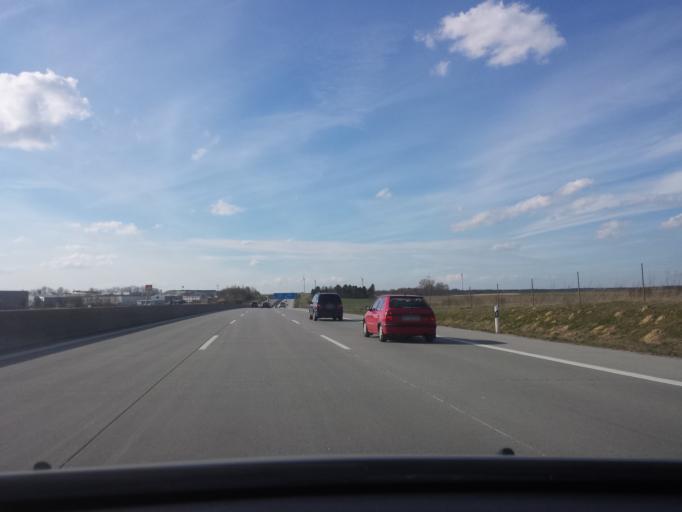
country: DE
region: Bavaria
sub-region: Upper Bavaria
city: Odelzhausen
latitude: 48.3010
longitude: 11.2177
